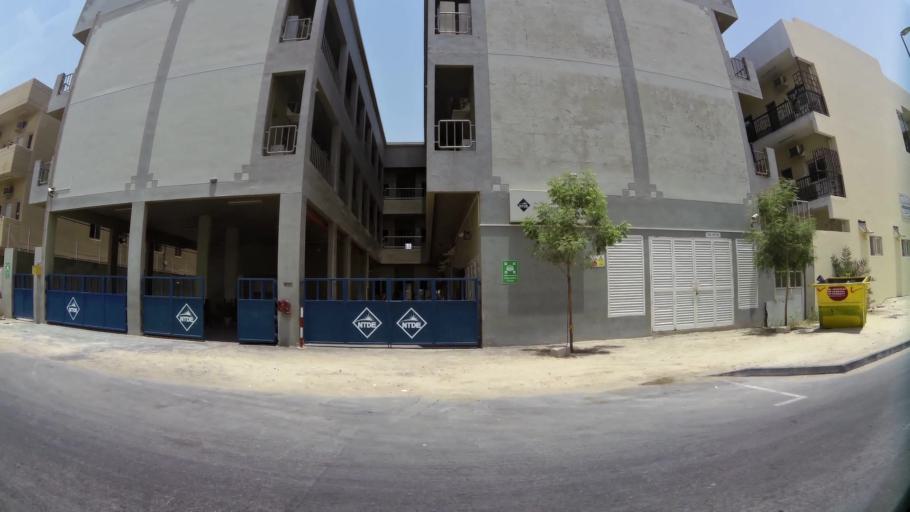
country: AE
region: Ash Shariqah
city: Sharjah
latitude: 25.2674
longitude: 55.4321
